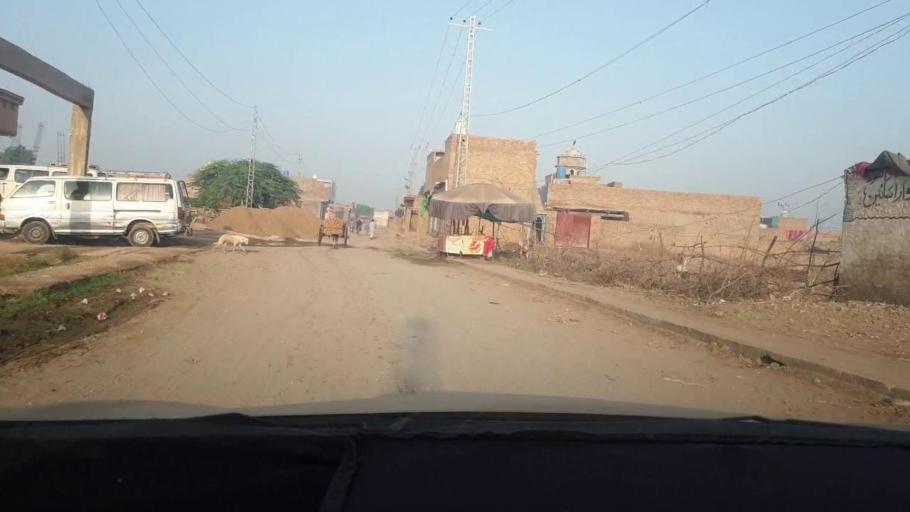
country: PK
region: Sindh
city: Larkana
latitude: 27.5411
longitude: 68.2220
